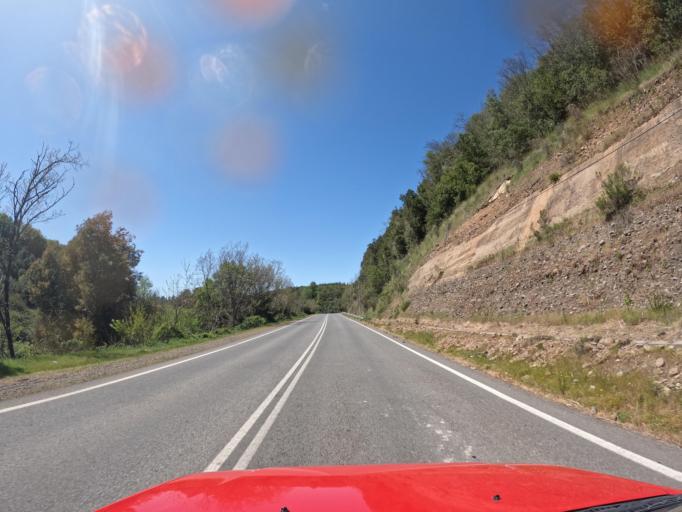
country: CL
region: Maule
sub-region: Provincia de Talca
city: San Clemente
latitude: -35.4673
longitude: -71.2730
